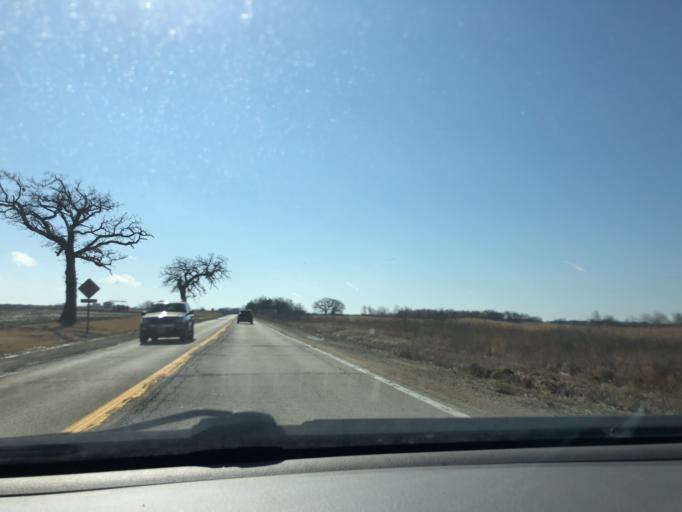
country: US
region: Illinois
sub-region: Kane County
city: Pingree Grove
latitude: 42.1031
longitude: -88.4547
